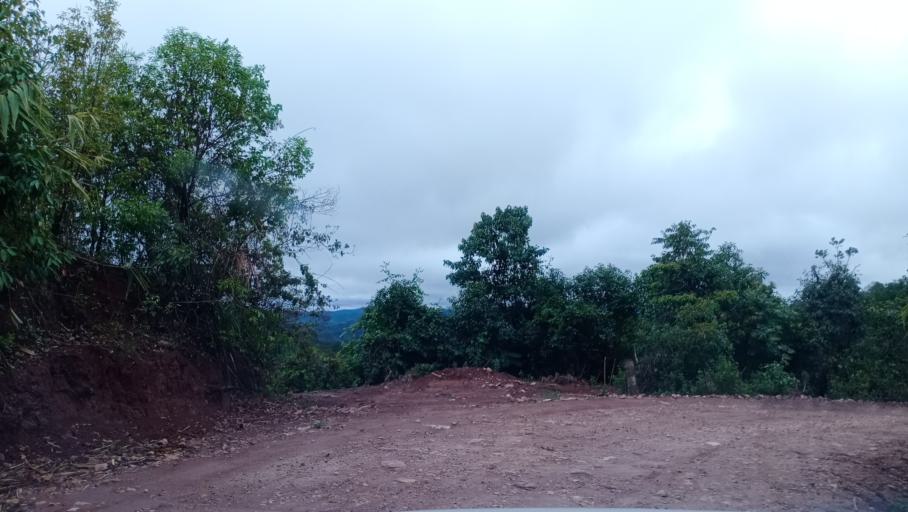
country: LA
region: Phongsali
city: Phongsali
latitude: 21.3430
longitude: 102.0761
